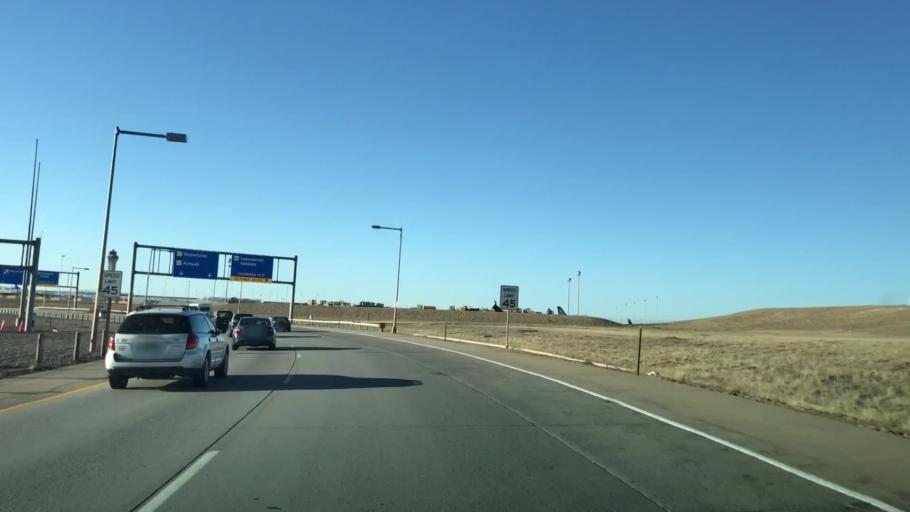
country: US
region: Colorado
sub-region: Weld County
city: Lochbuie
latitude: 39.8493
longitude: -104.6655
